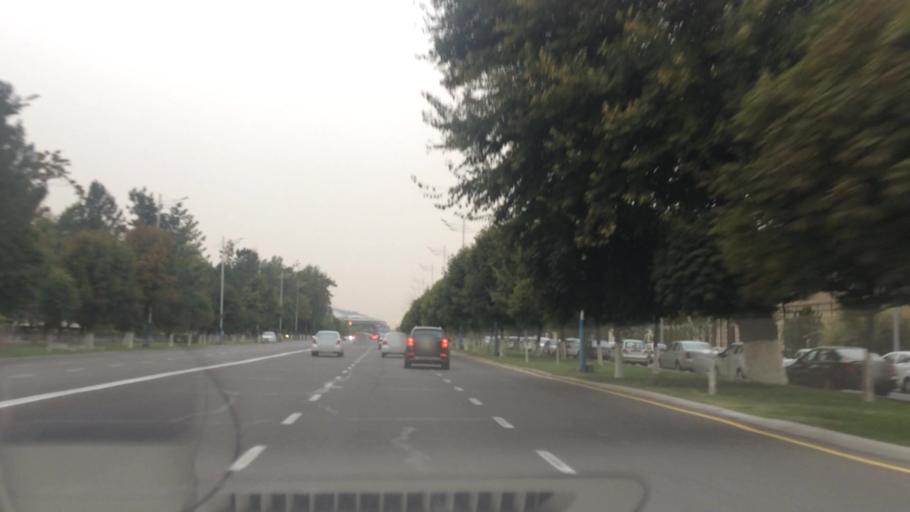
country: UZ
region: Toshkent Shahri
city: Tashkent
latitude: 41.3060
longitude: 69.2626
